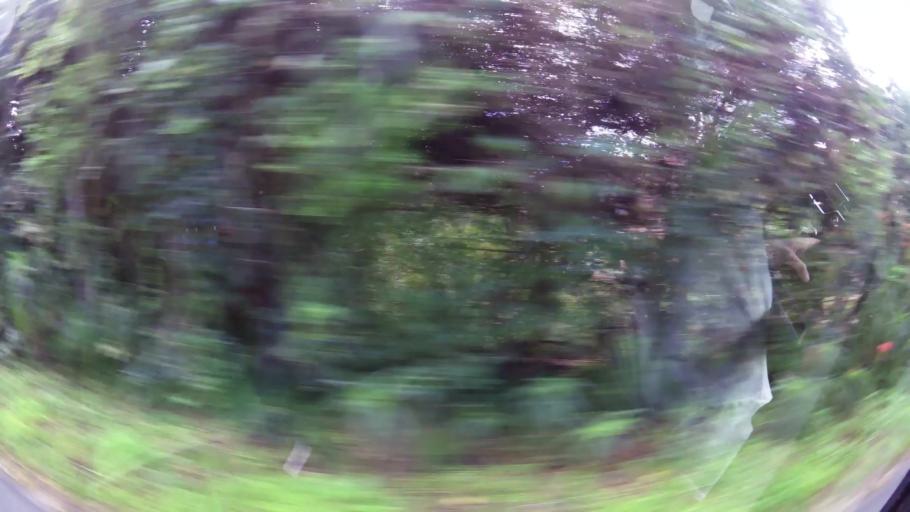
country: ZA
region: Western Cape
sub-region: Eden District Municipality
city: Knysna
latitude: -34.0553
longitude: 23.0785
